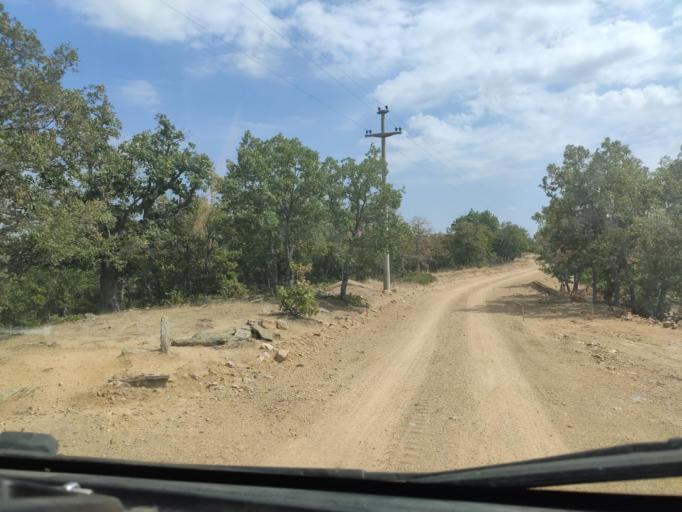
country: MK
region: Radovis
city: Radovish
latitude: 41.6667
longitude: 22.4073
